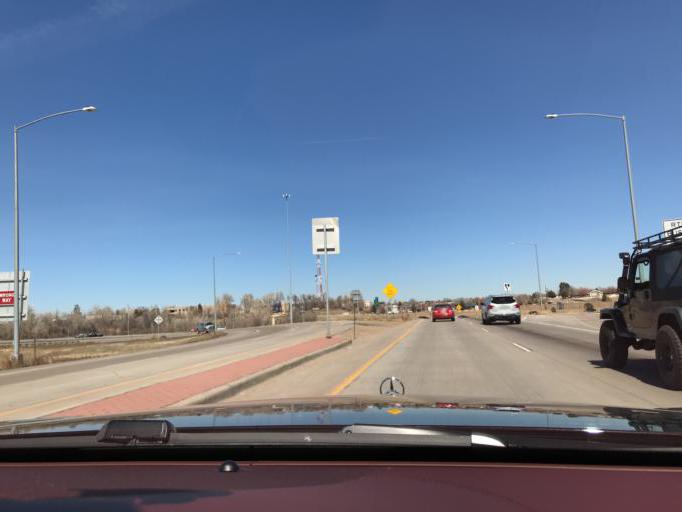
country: US
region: Colorado
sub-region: Jefferson County
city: Applewood
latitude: 39.7796
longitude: -105.1325
